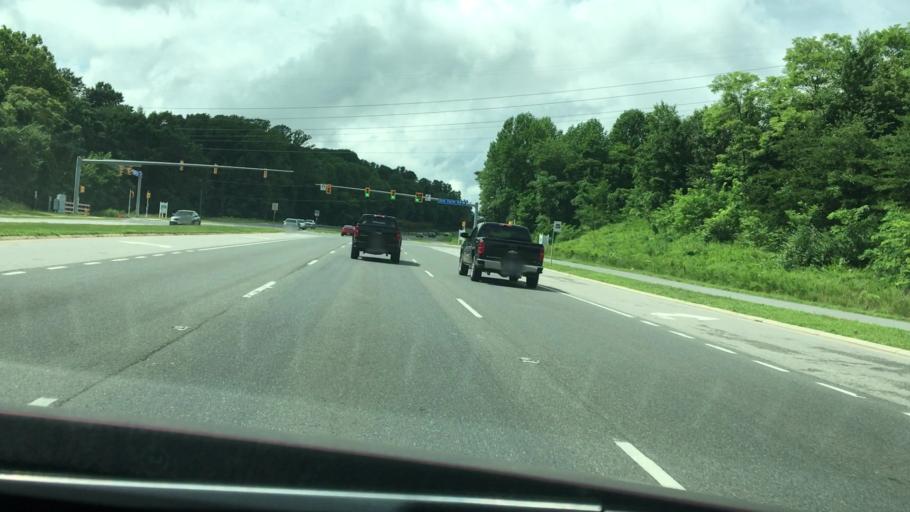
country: US
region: Virginia
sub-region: Prince William County
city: Dale City
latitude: 38.6594
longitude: -77.3236
